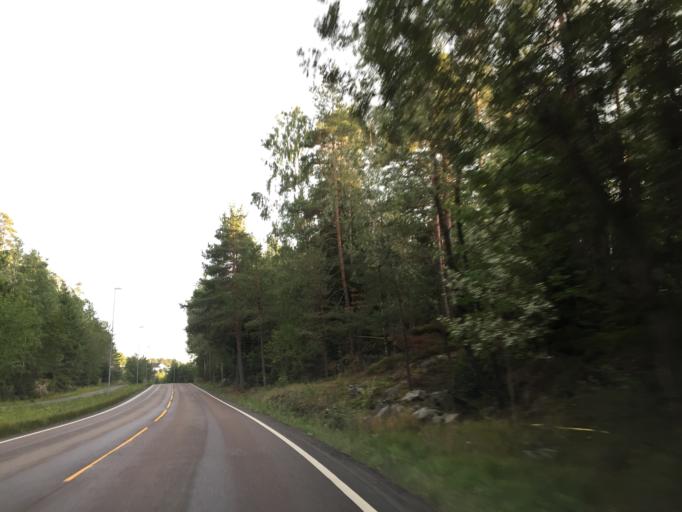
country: NO
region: Akershus
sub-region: Ski
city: Ski
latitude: 59.7696
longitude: 10.8490
